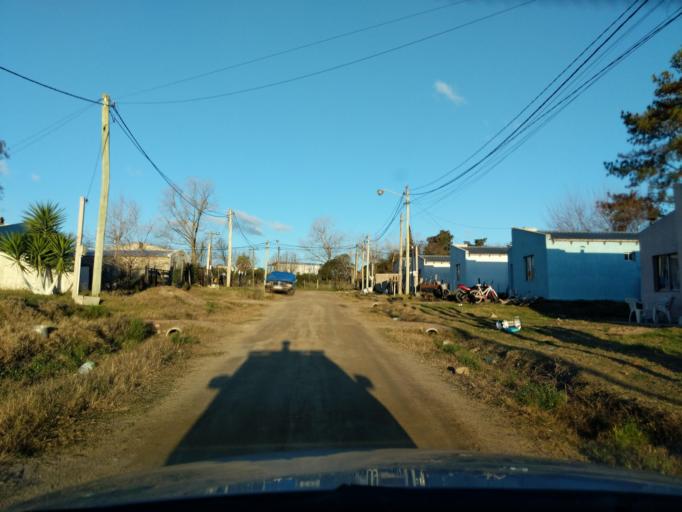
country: UY
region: Florida
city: Florida
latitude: -34.1038
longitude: -56.2368
